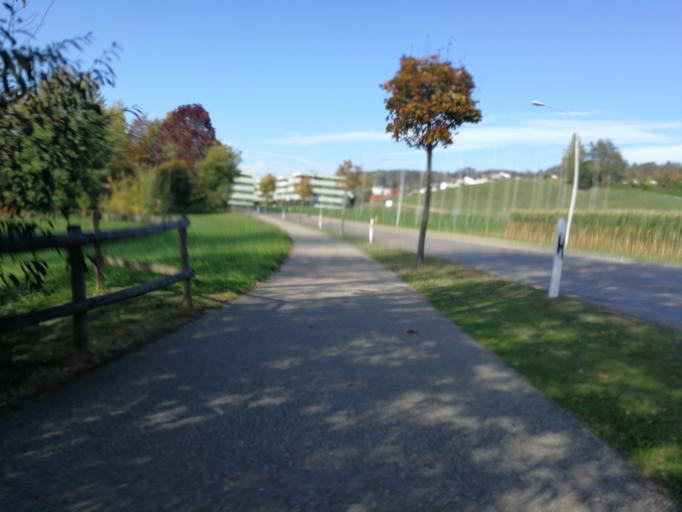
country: CH
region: Zurich
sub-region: Bezirk Hinwil
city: Hinwil
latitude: 47.2948
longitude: 8.8516
